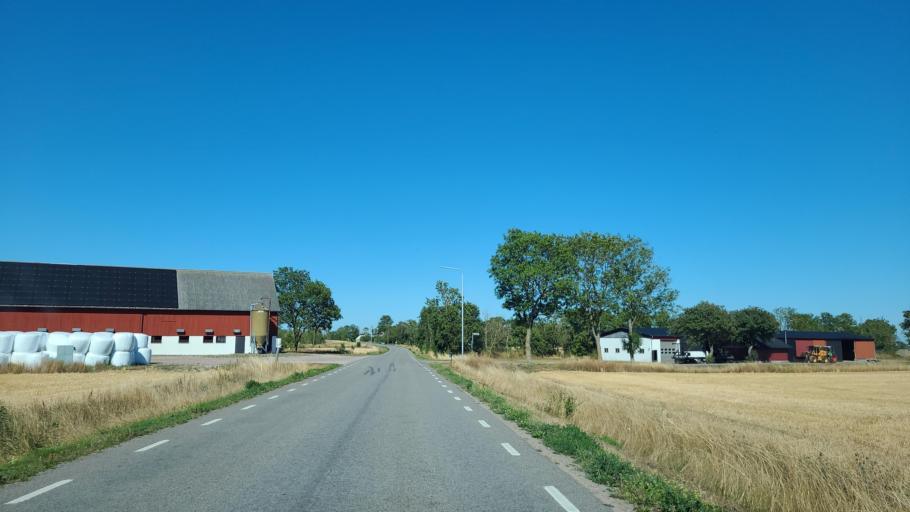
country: SE
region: Kalmar
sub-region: Borgholms Kommun
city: Borgholm
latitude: 56.8957
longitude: 16.8270
